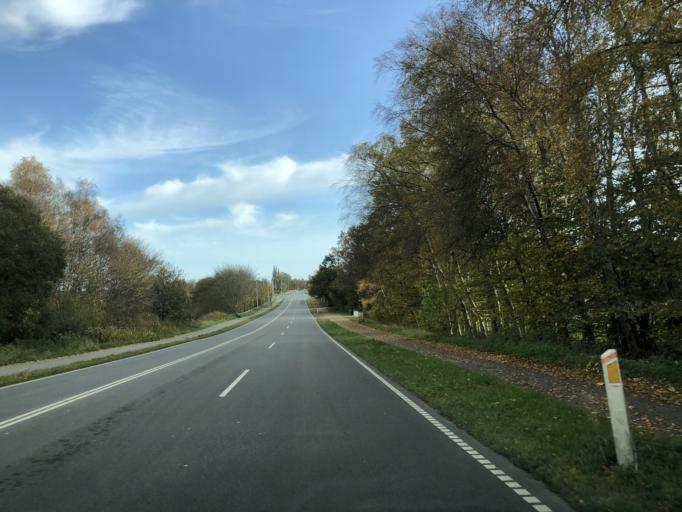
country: DK
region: Capital Region
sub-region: Rudersdal Kommune
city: Birkerod
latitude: 55.8546
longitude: 12.4121
